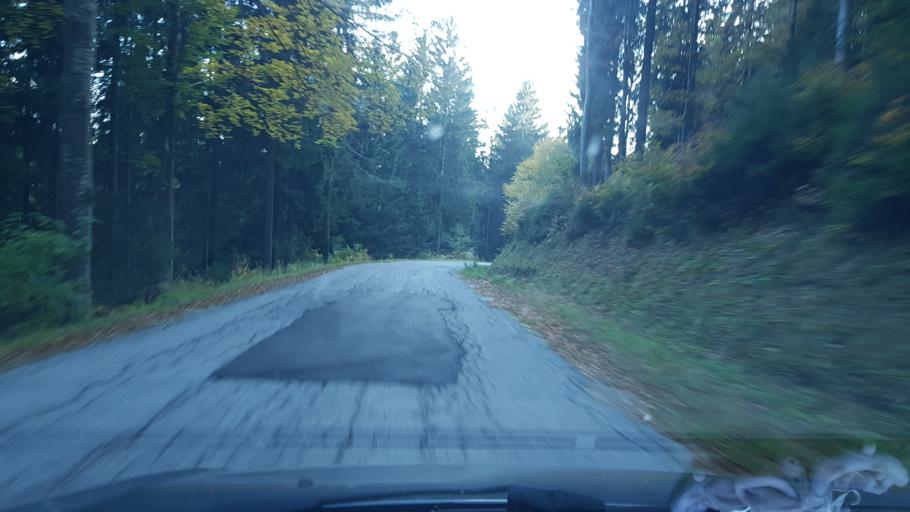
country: SI
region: Slovenj Gradec
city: Legen
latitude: 46.4958
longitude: 15.1862
